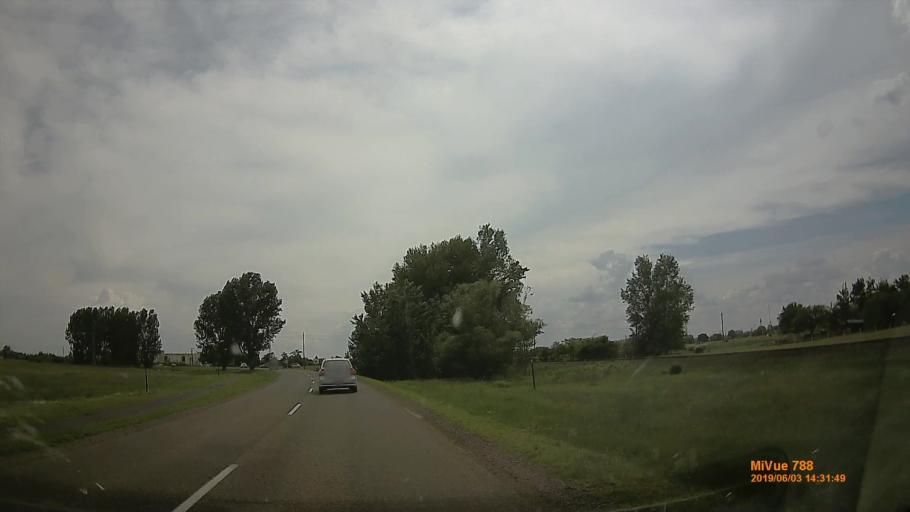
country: HU
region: Bacs-Kiskun
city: Tiszakecske
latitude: 46.9597
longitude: 20.0922
